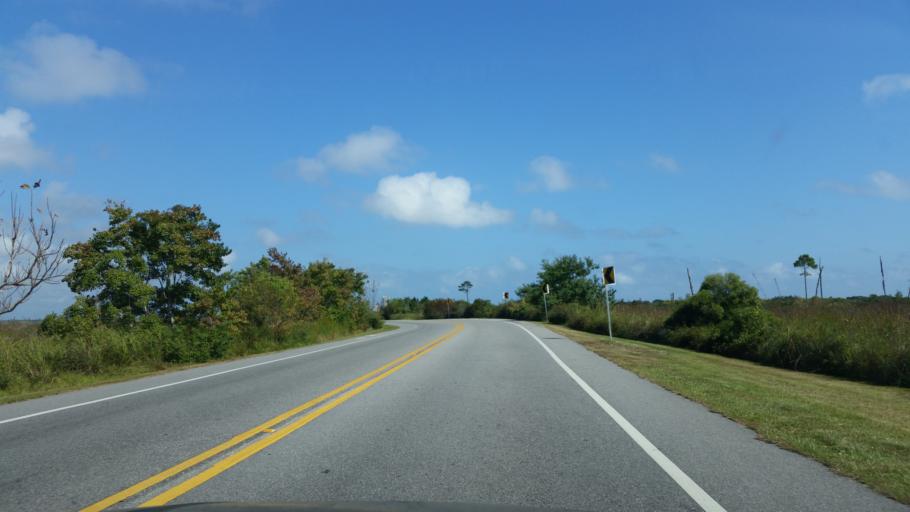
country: US
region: Alabama
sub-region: Baldwin County
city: Gulf Shores
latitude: 30.2557
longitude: -87.6766
